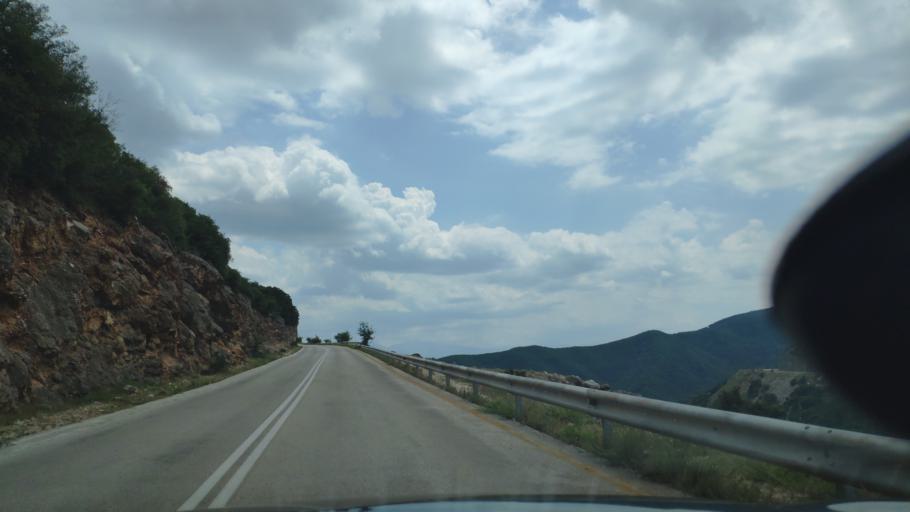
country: GR
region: Epirus
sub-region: Nomos Artas
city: Kampi
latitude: 39.2762
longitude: 20.9689
